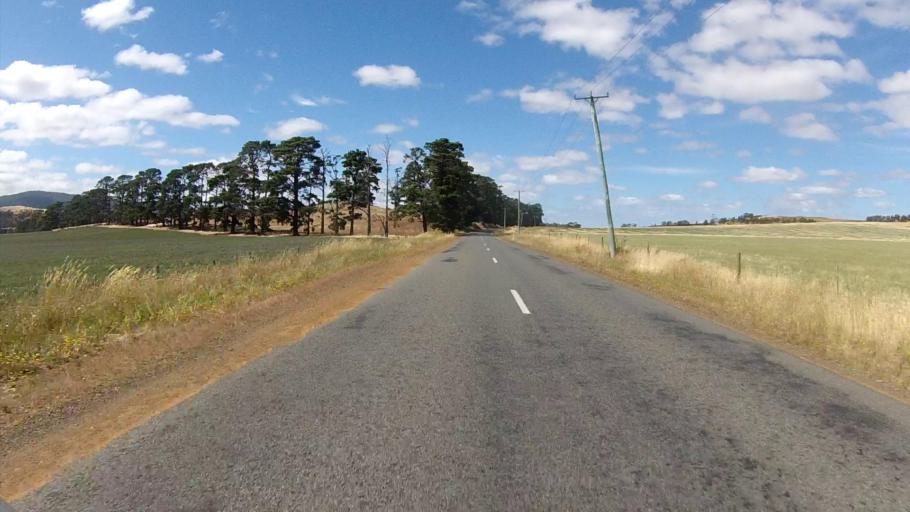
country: AU
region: Tasmania
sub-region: Sorell
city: Sorell
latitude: -42.6361
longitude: 147.4314
